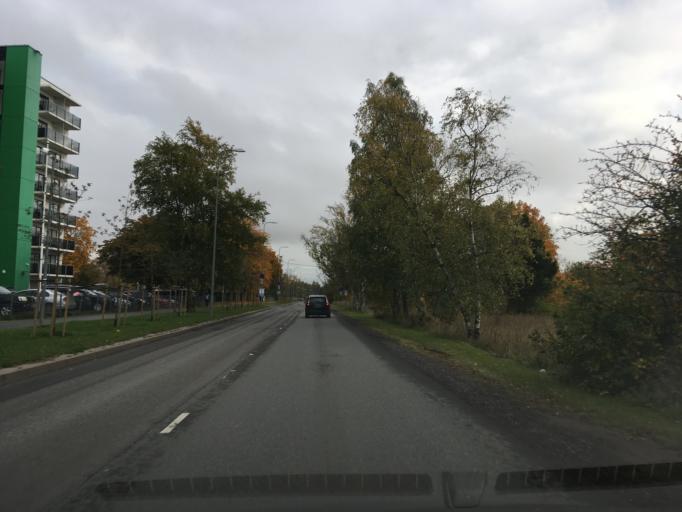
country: EE
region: Harju
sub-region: Viimsi vald
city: Viimsi
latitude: 59.4466
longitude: 24.8251
